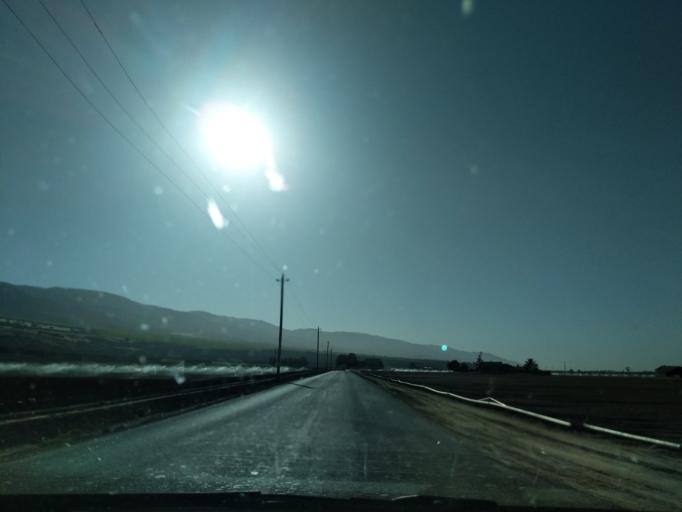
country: US
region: California
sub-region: Monterey County
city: Soledad
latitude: 36.4071
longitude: -121.3697
